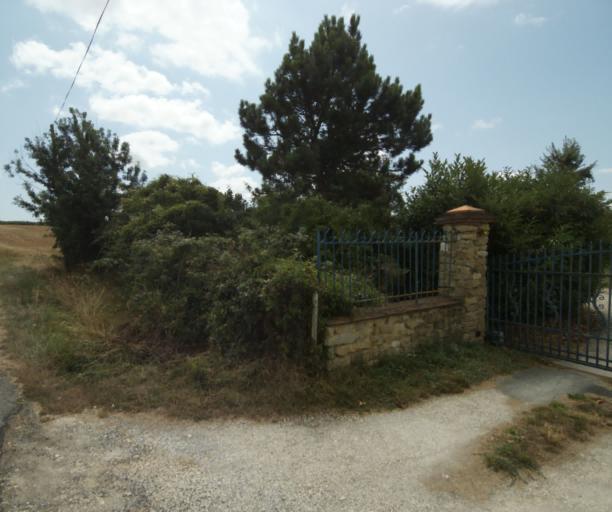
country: FR
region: Midi-Pyrenees
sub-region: Departement de la Haute-Garonne
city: Saint-Felix-Lauragais
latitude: 43.4052
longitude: 1.8985
